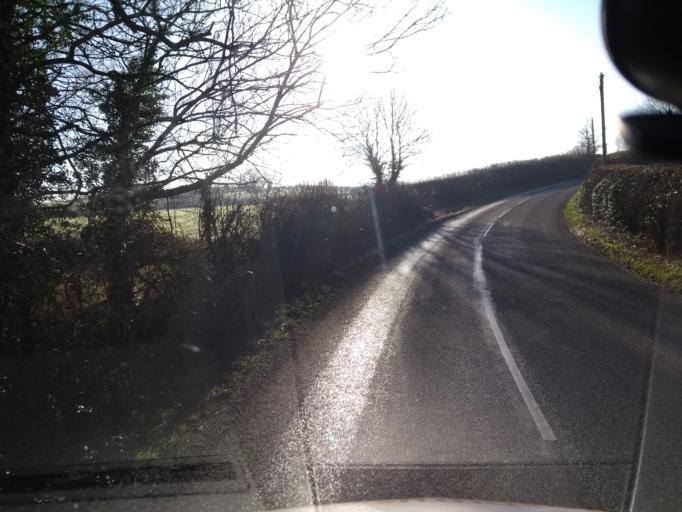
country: GB
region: England
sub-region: Somerset
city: Redlynch
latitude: 51.0901
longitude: -2.4150
